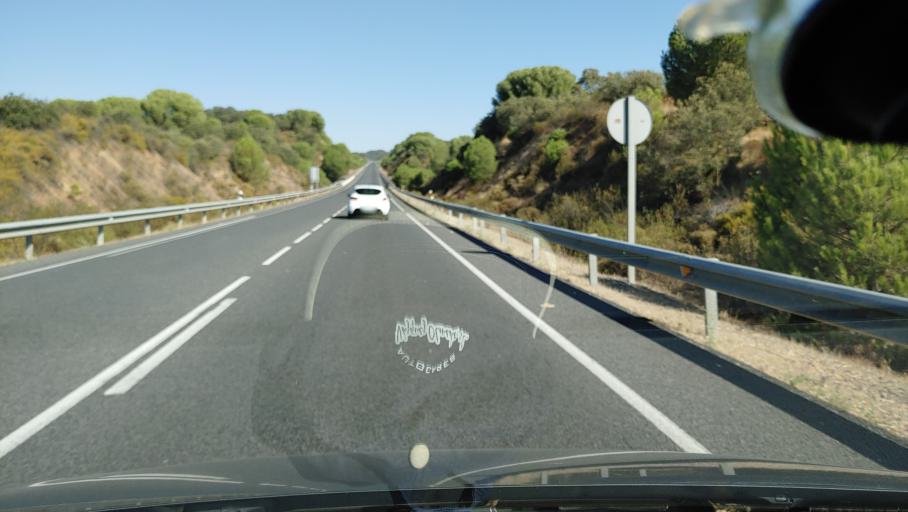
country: ES
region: Andalusia
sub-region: Province of Cordoba
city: Cordoba
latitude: 38.0026
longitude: -4.7995
